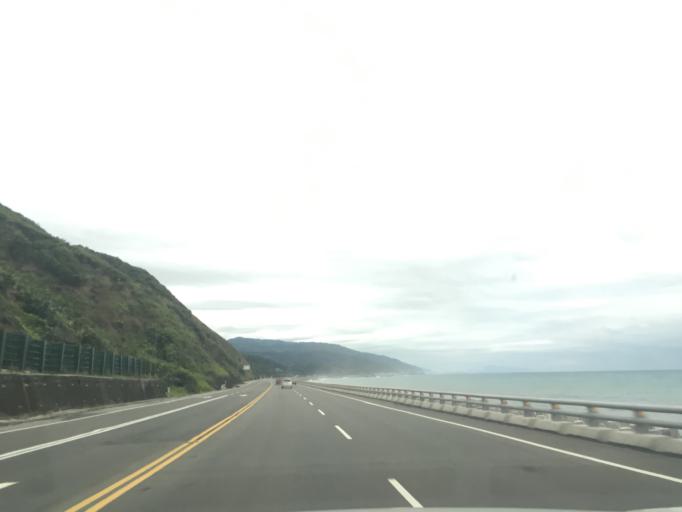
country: TW
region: Taiwan
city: Hengchun
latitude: 22.3111
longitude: 120.8911
